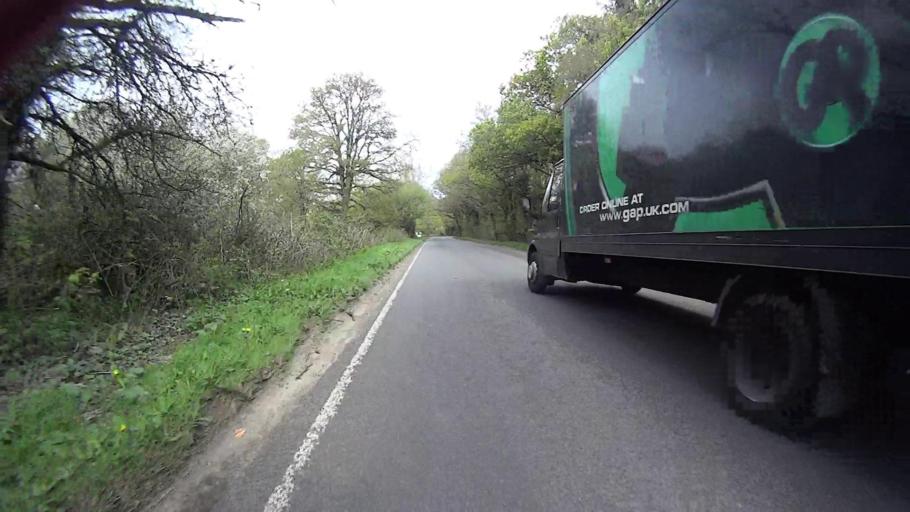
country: GB
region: England
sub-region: West Sussex
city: Gossops Green
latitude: 51.1364
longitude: -0.2259
